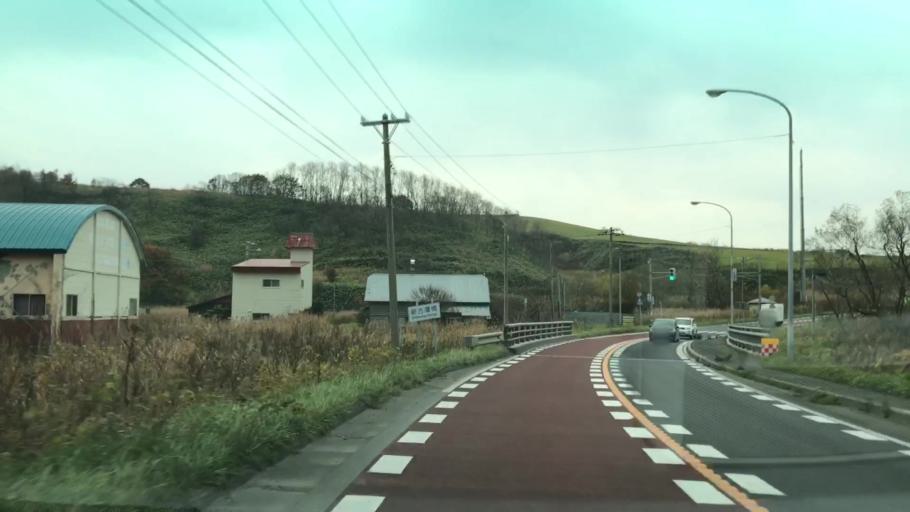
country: JP
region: Hokkaido
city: Ishikari
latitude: 43.3560
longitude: 141.4304
